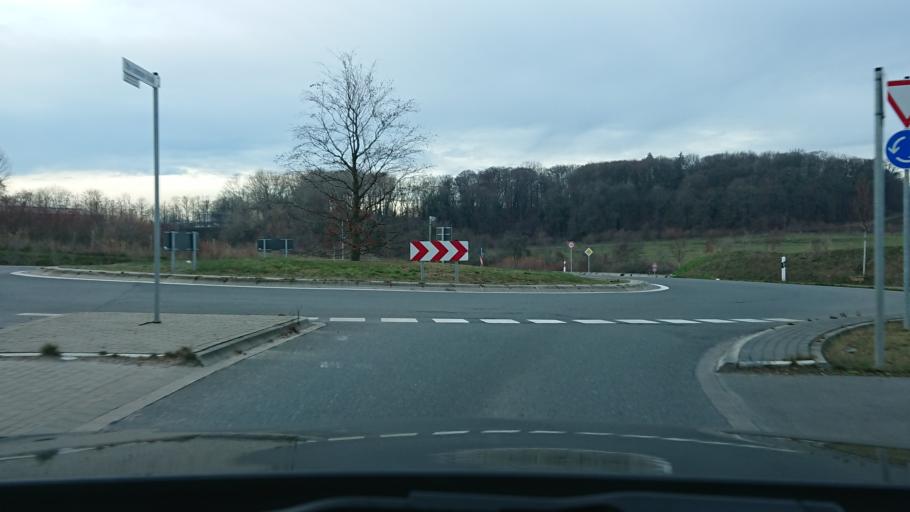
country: DE
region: North Rhine-Westphalia
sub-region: Regierungsbezirk Koln
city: Frechen
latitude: 50.9213
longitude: 6.7953
